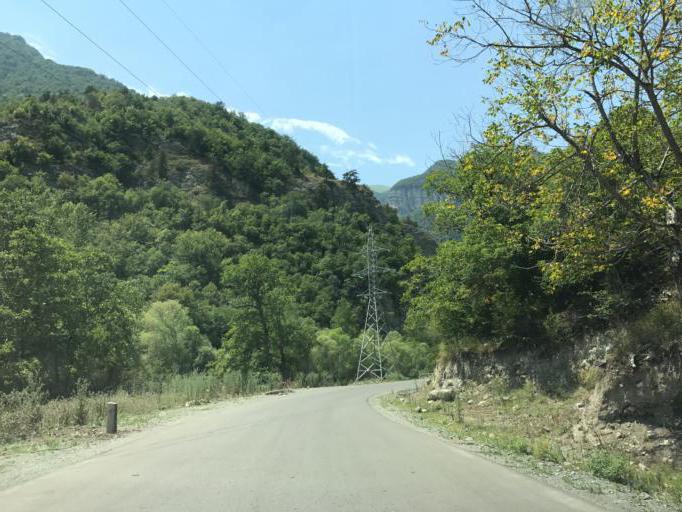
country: AZ
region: Kalbacar Rayonu
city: Kerbakhiar
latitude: 40.1450
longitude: 46.3018
